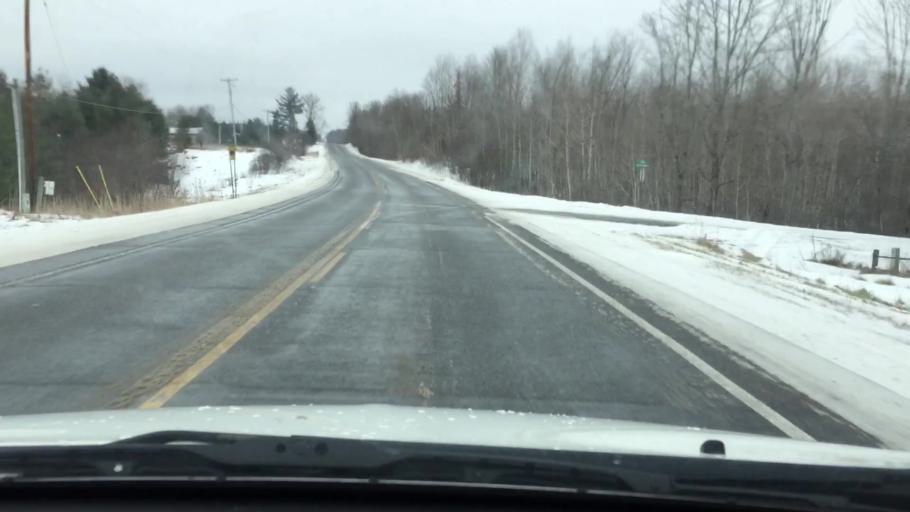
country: US
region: Michigan
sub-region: Wexford County
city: Cadillac
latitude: 44.1135
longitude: -85.4442
